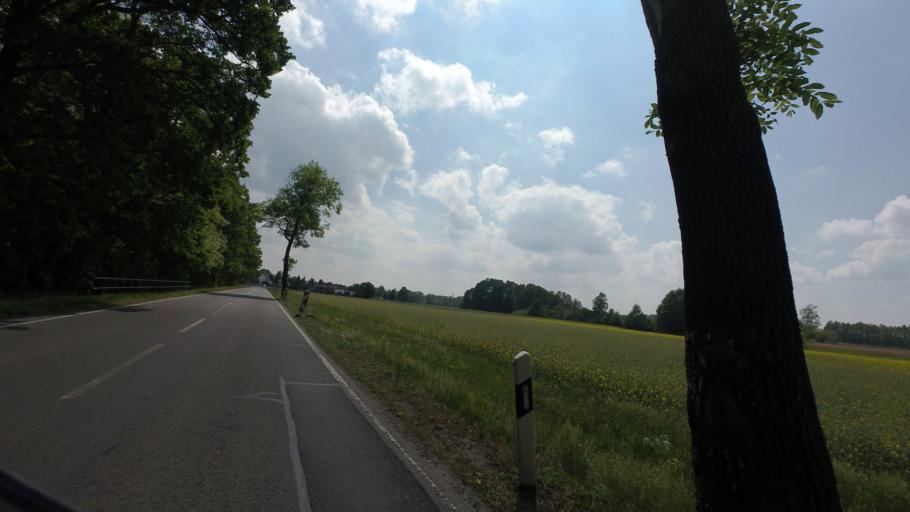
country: DE
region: Saxony
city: Rietschen
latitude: 51.4070
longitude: 14.7869
